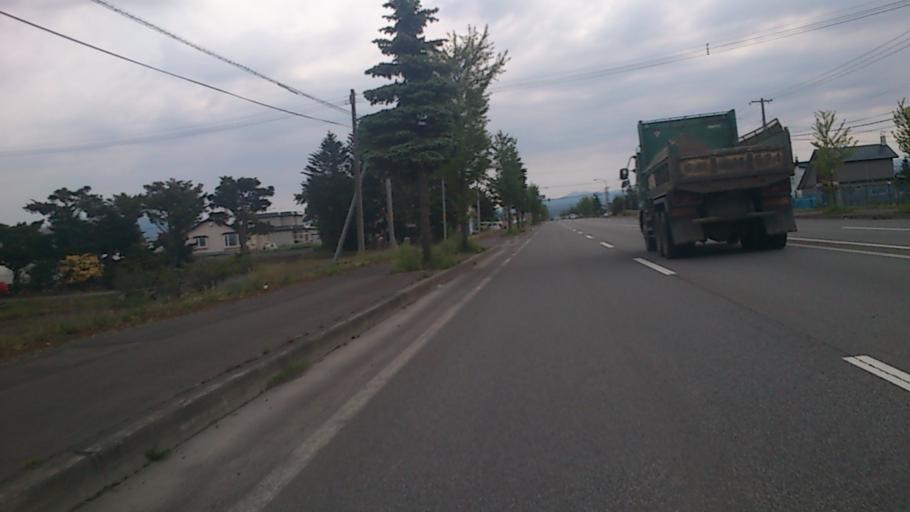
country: JP
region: Hokkaido
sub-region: Asahikawa-shi
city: Asahikawa
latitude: 43.8370
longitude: 142.4763
